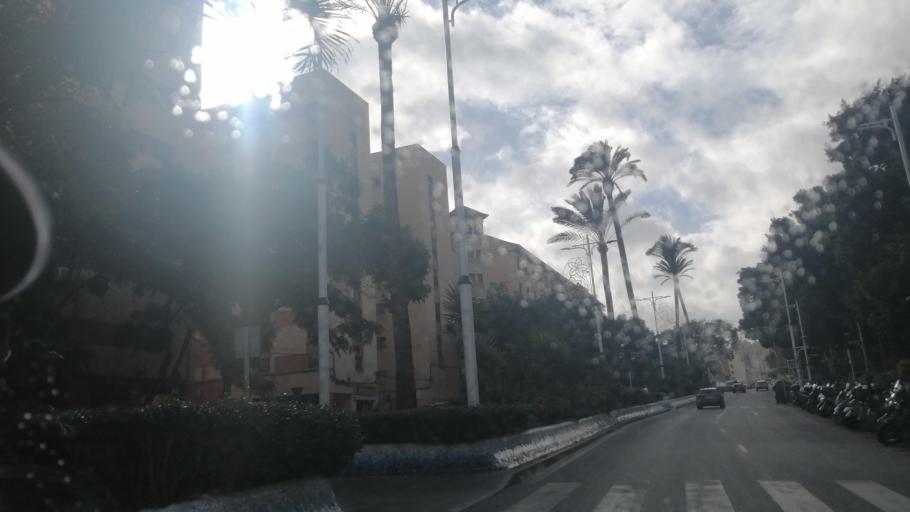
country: ES
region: Ceuta
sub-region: Ceuta
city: Ceuta
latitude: 35.8894
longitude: -5.3215
